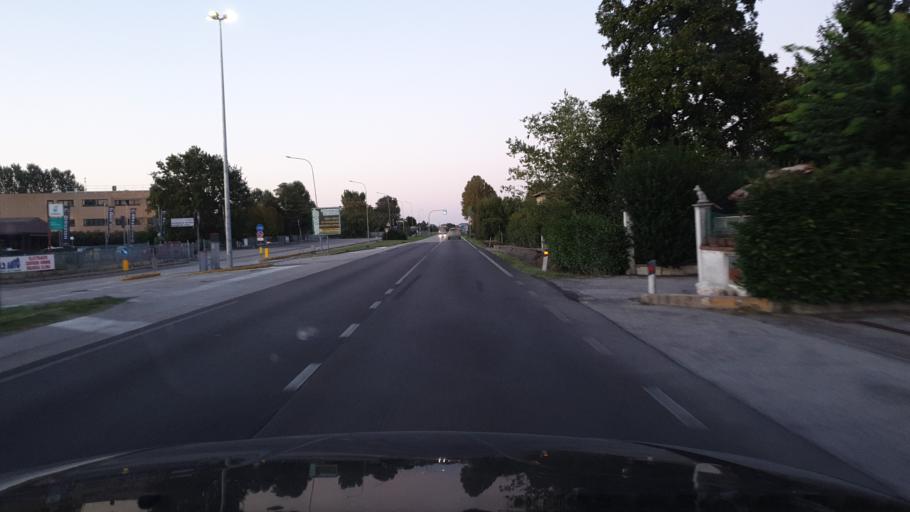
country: IT
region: Emilia-Romagna
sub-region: Provincia di Bologna
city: Altedo
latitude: 44.6785
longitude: 11.4945
